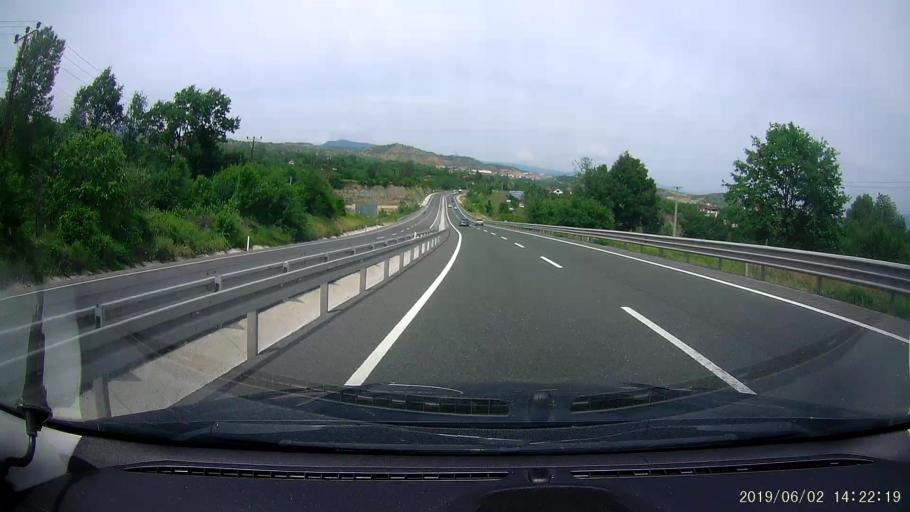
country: TR
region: Kastamonu
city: Tosya
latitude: 40.9912
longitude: 34.0147
